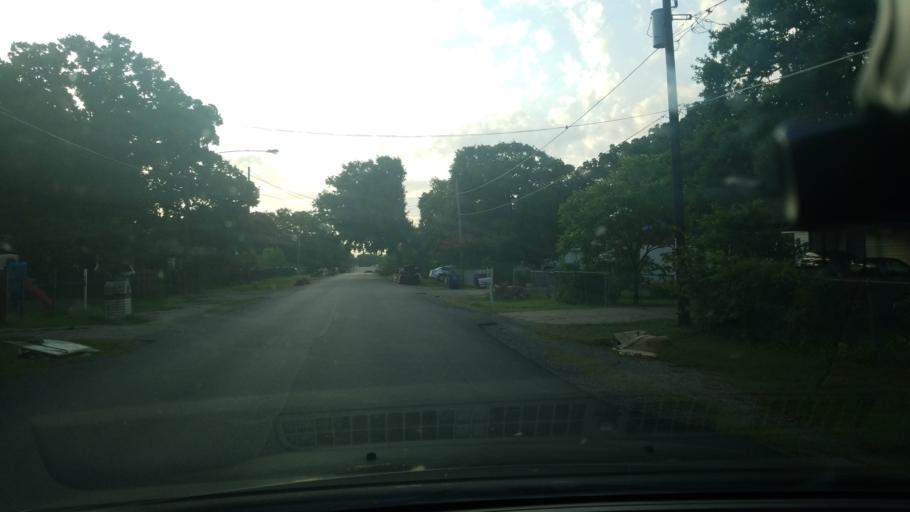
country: US
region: Texas
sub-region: Dallas County
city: Balch Springs
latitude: 32.7277
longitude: -96.6566
